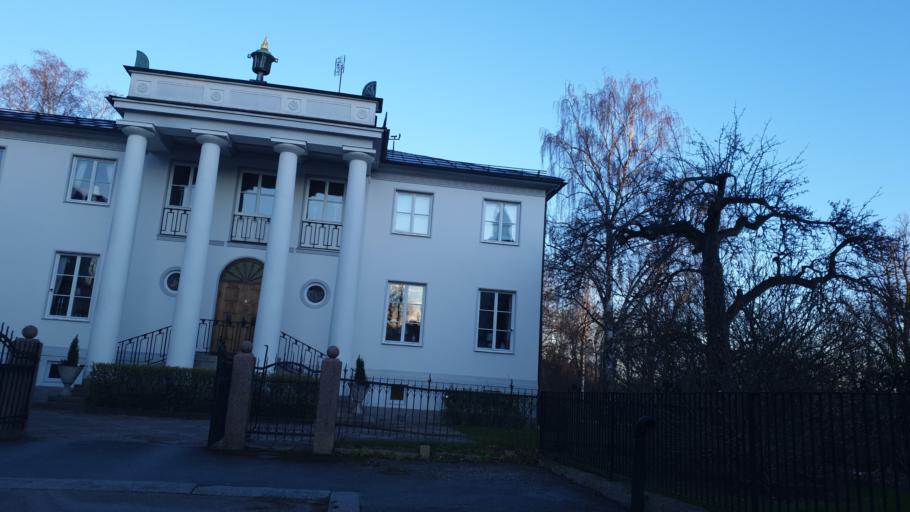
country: SE
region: OErebro
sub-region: Orebro Kommun
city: Orebro
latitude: 59.2732
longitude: 15.2245
